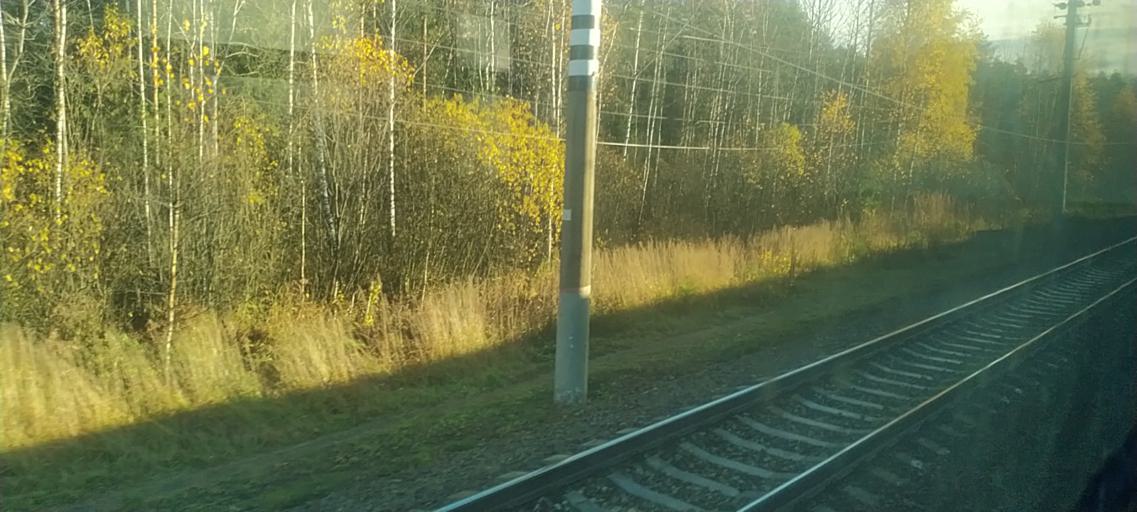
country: RU
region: Moskovskaya
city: Ramenskoye
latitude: 55.6389
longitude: 38.2589
